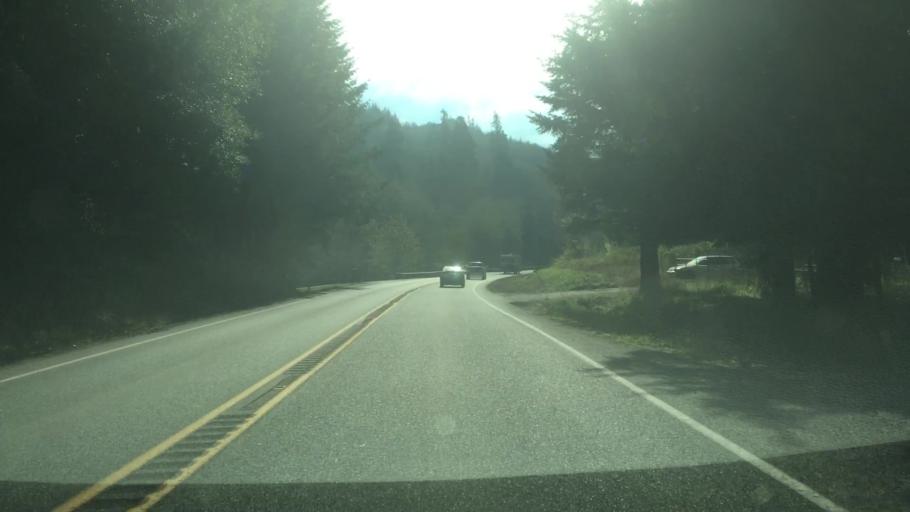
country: US
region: Washington
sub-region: Grays Harbor County
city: Montesano
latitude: 46.9520
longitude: -123.6120
